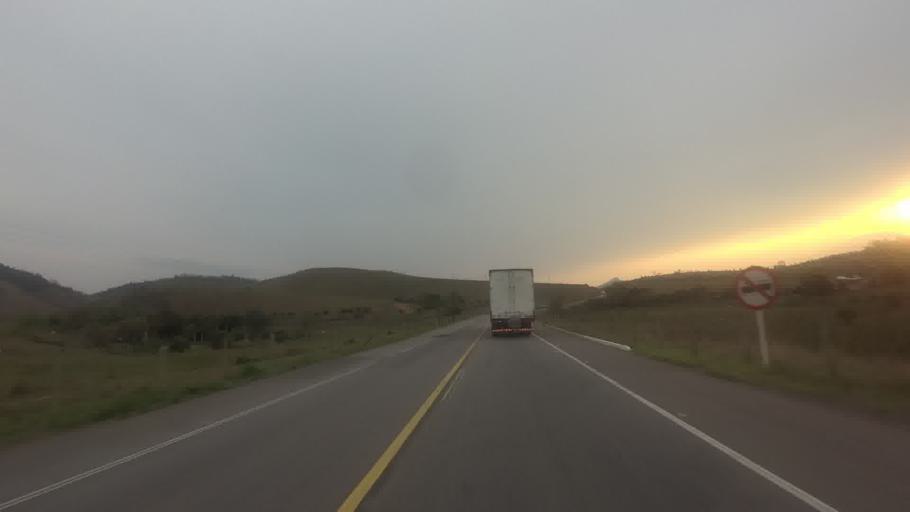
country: BR
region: Minas Gerais
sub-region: Recreio
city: Recreio
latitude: -21.6856
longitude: -42.4030
